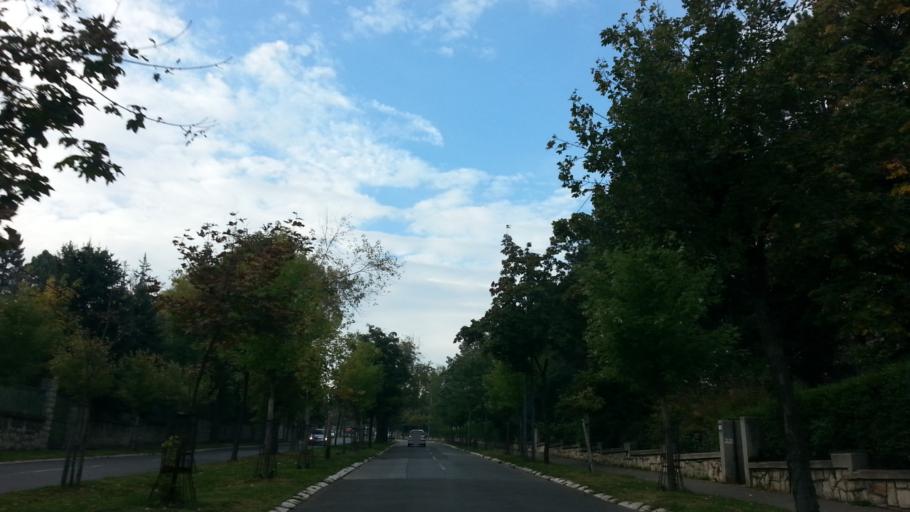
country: RS
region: Central Serbia
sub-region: Belgrade
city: Savski Venac
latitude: 44.7743
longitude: 20.4559
